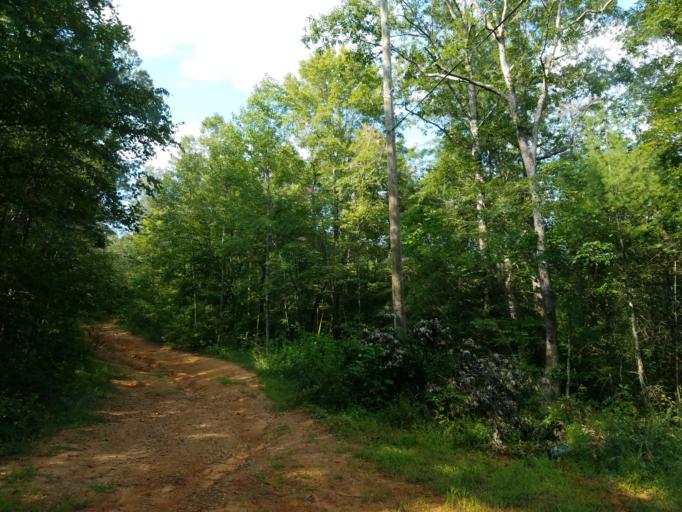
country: US
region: Georgia
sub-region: Fannin County
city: Blue Ridge
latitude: 34.7933
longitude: -84.4084
